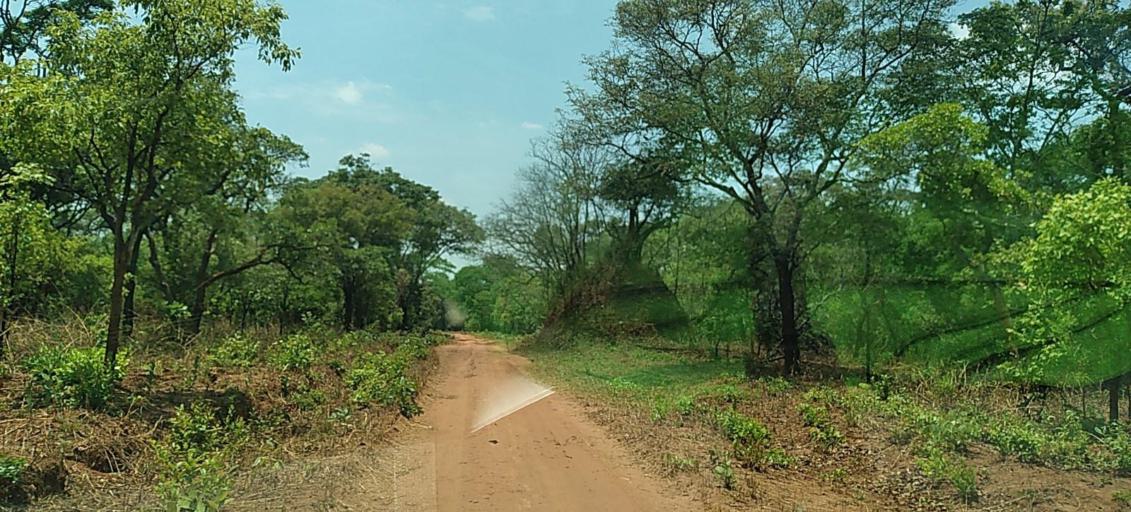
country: CD
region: Katanga
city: Kolwezi
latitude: -11.3552
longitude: 25.2104
